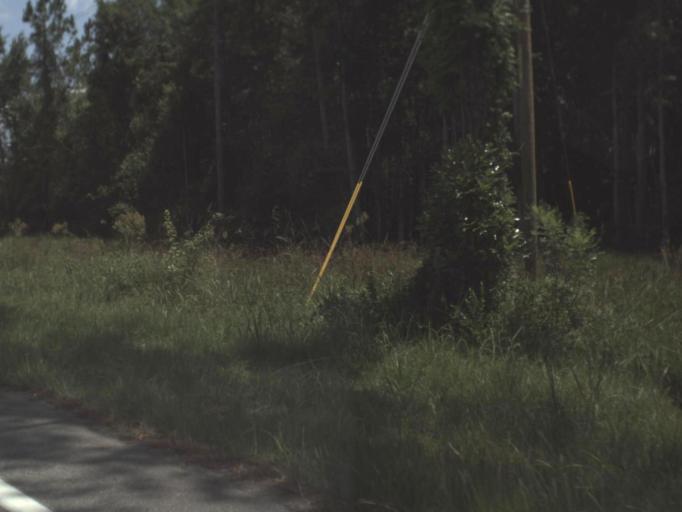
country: US
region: Florida
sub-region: Madison County
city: Madison
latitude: 30.5040
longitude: -83.6327
